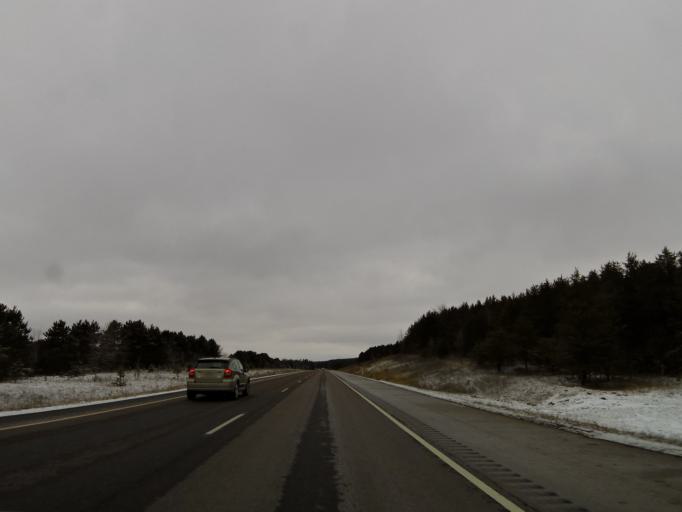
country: US
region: Wisconsin
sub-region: Trempealeau County
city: Osseo
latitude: 44.5552
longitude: -91.1722
